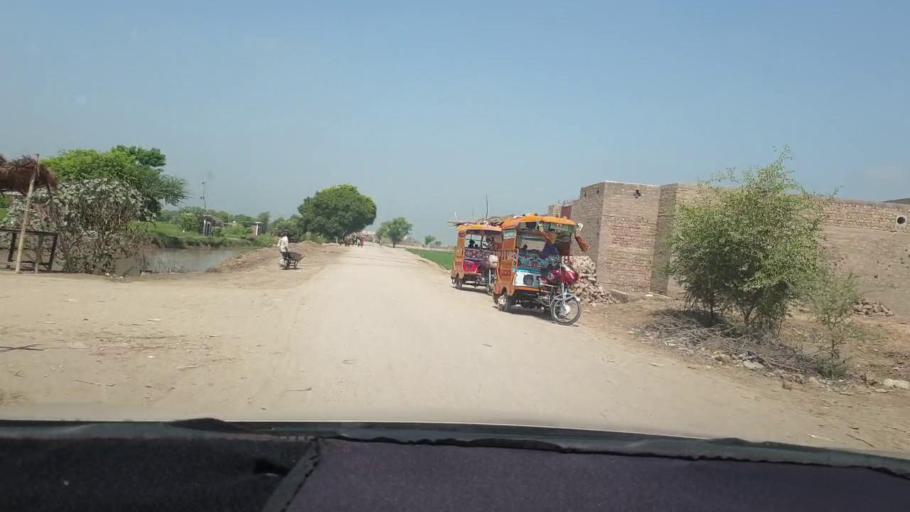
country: PK
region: Sindh
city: Miro Khan
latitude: 27.7715
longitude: 68.0615
